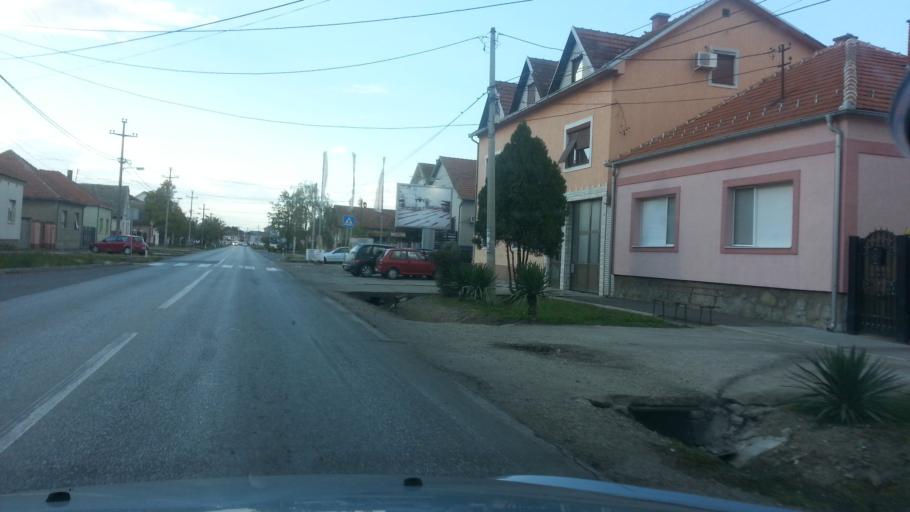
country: RS
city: Novi Banovci
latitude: 44.9105
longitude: 20.2673
